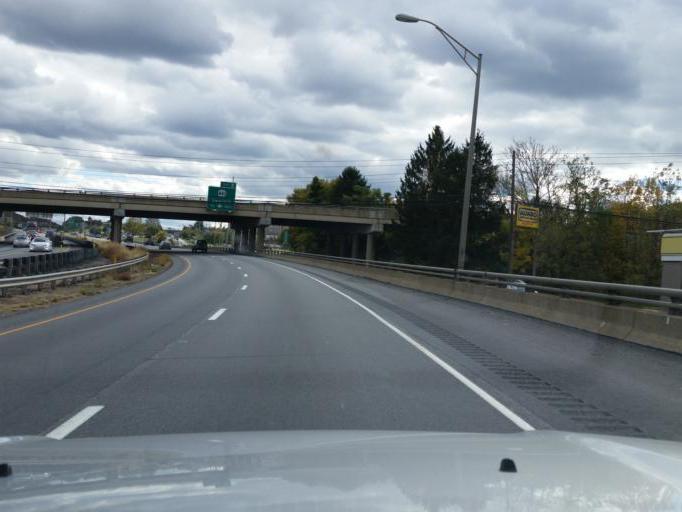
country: US
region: Pennsylvania
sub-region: Dauphin County
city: Lawnton
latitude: 40.2489
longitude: -76.8129
